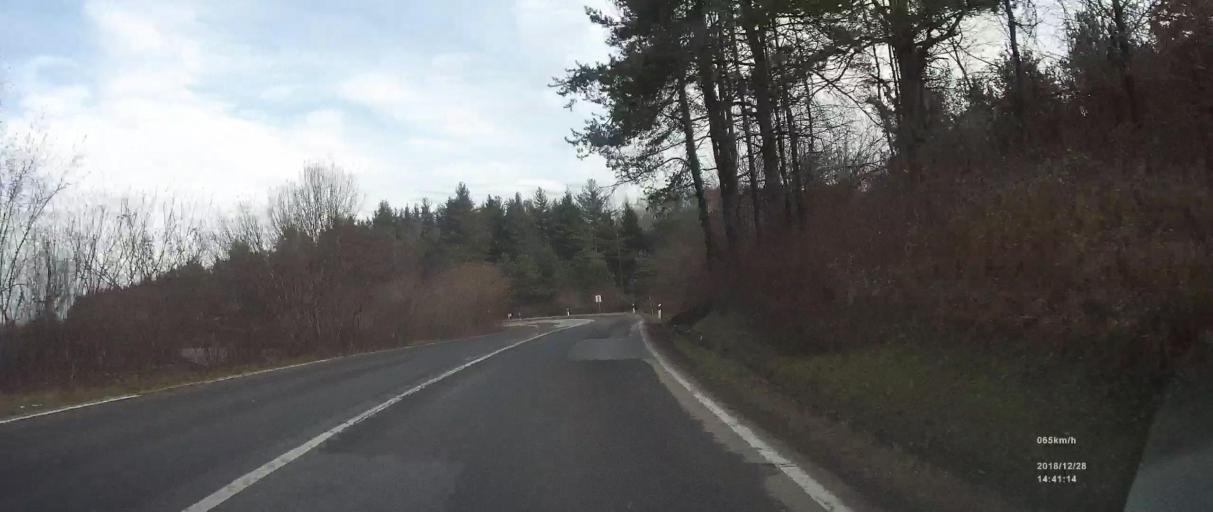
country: SI
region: Crnomelj
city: Crnomelj
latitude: 45.4362
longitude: 15.2546
